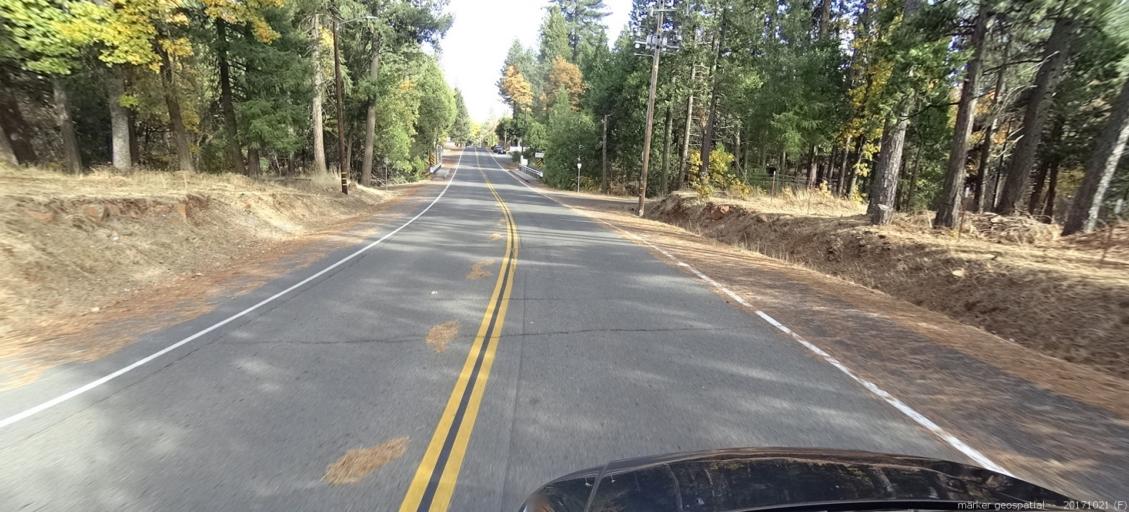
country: US
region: California
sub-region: Shasta County
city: Burney
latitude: 40.8761
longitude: -121.6718
